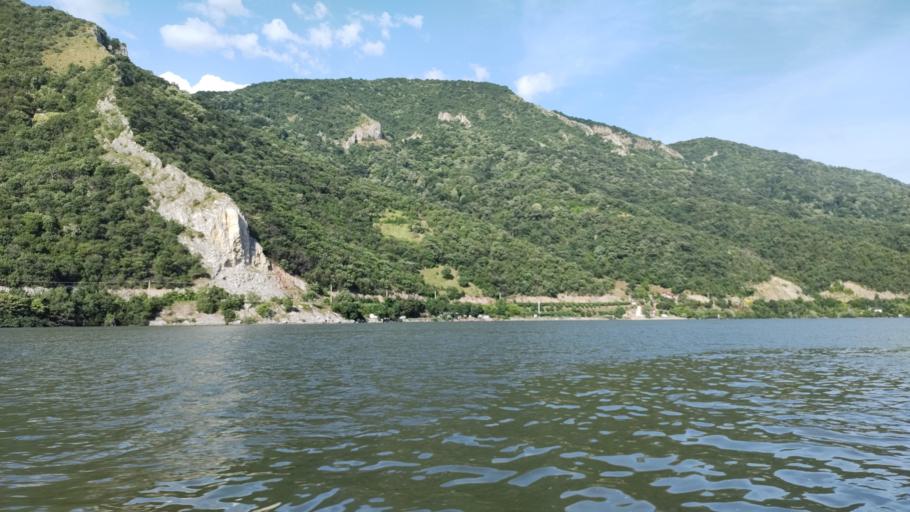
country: RO
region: Caras-Severin
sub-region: Comuna Berzasca
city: Berzasca
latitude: 44.5983
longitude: 22.0188
